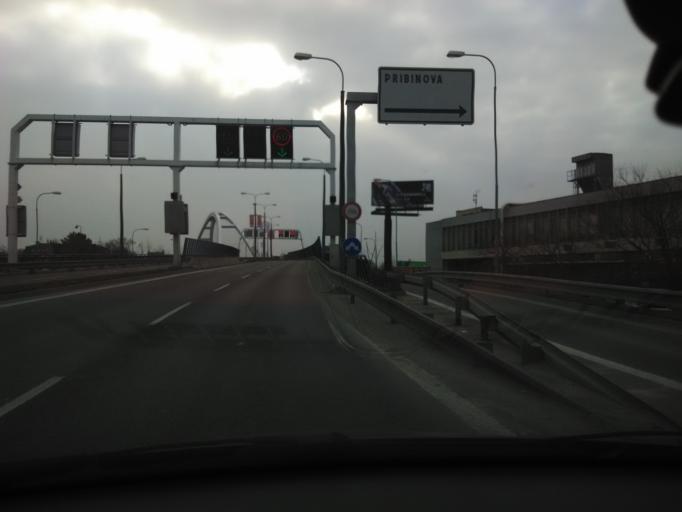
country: SK
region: Bratislavsky
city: Bratislava
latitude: 48.1414
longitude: 17.1295
